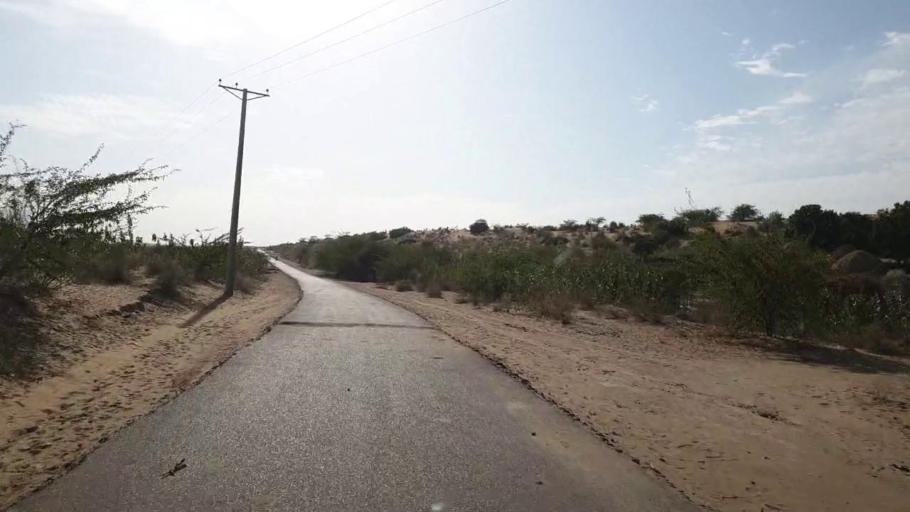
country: PK
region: Sindh
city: Nabisar
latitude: 25.0427
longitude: 70.0067
